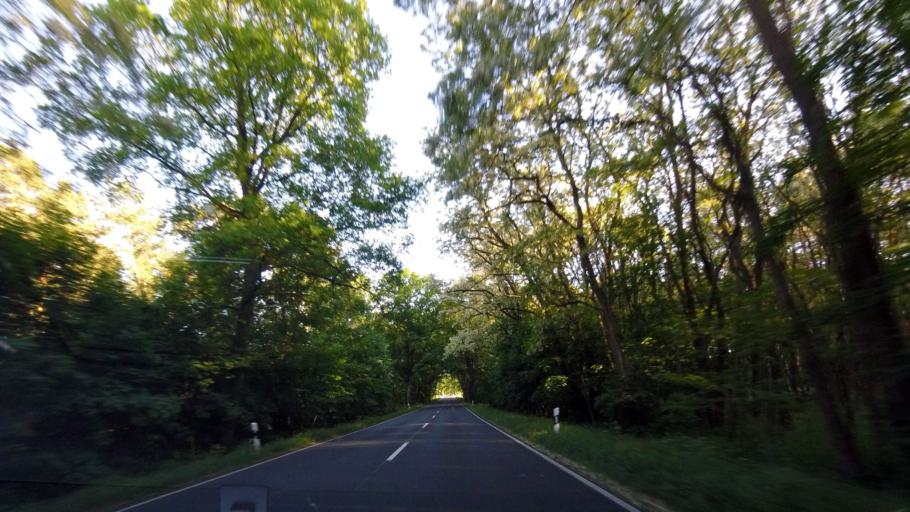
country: DE
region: Brandenburg
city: Golzow
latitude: 52.3184
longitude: 12.6078
